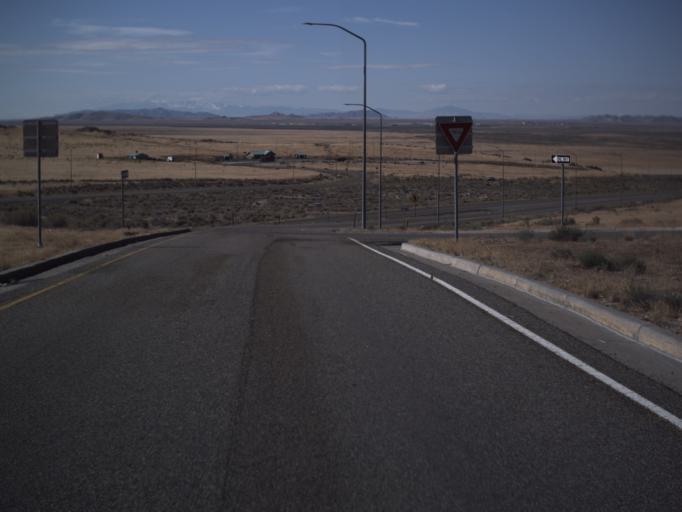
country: US
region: Utah
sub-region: Tooele County
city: Grantsville
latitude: 40.7616
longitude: -113.0110
